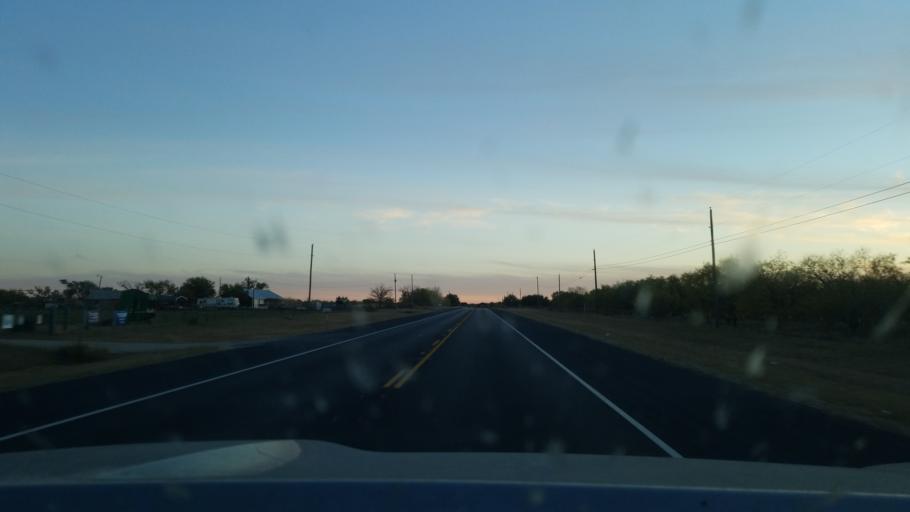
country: US
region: Texas
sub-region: Stephens County
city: Breckenridge
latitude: 32.6323
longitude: -98.9028
